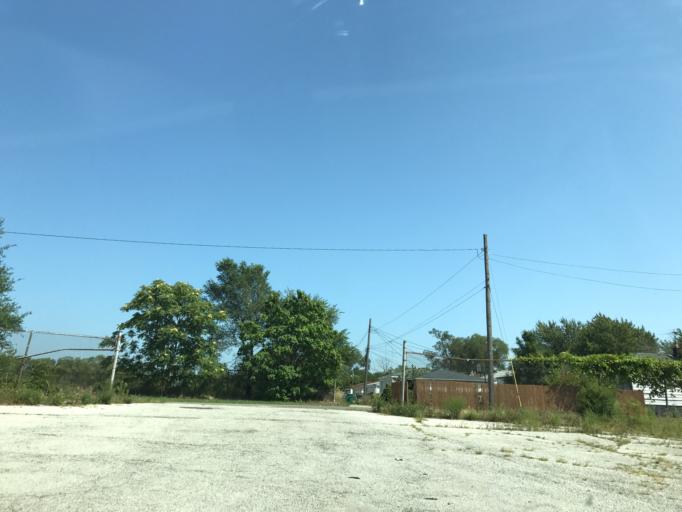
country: US
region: Indiana
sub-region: Lake County
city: Gary
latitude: 41.5784
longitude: -87.3445
